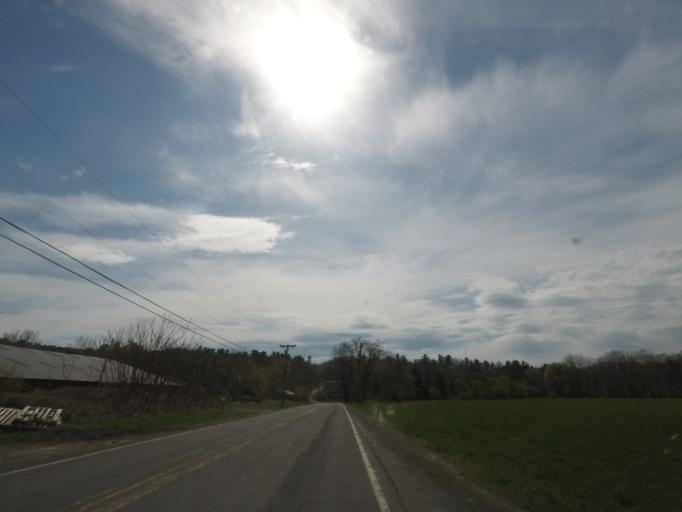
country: US
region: New York
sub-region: Columbia County
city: Chatham
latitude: 42.3487
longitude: -73.5722
